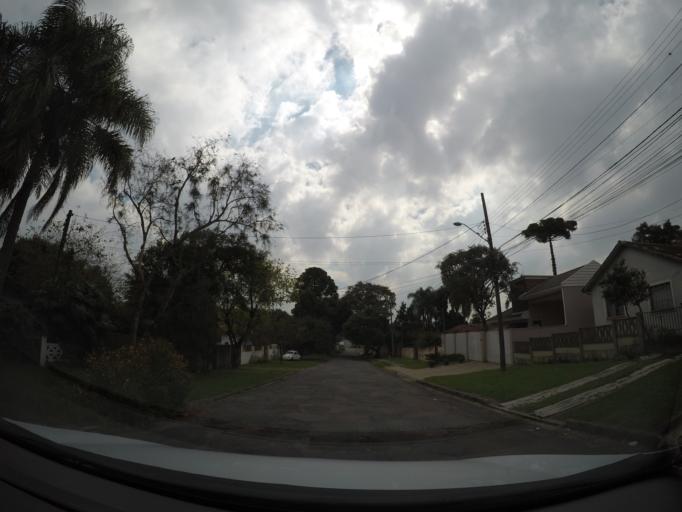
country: BR
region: Parana
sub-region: Sao Jose Dos Pinhais
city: Sao Jose dos Pinhais
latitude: -25.5020
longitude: -49.2470
